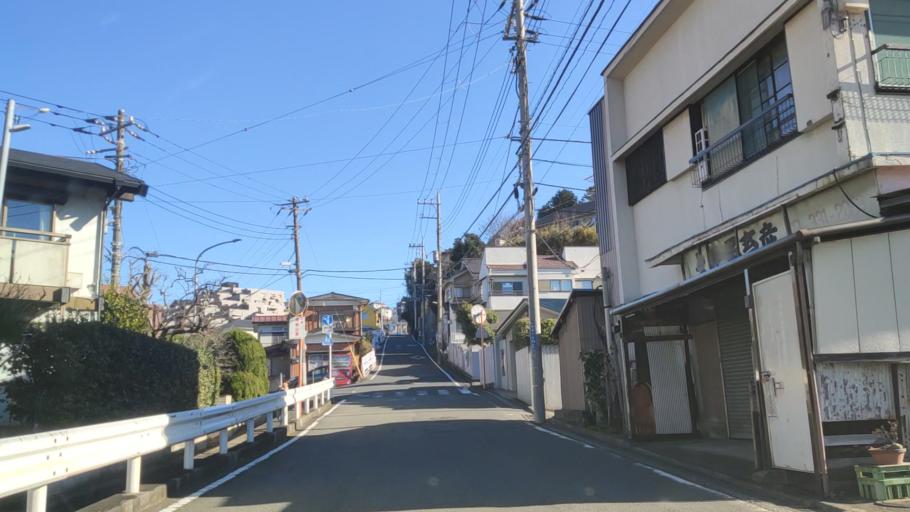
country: JP
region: Kanagawa
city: Yokohama
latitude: 35.4476
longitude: 139.5793
